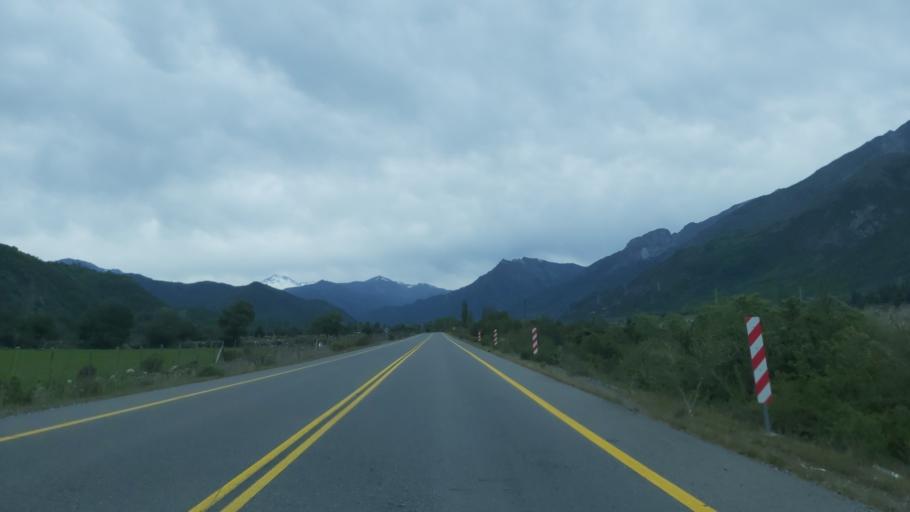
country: CL
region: Maule
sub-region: Provincia de Linares
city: Colbun
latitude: -35.7346
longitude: -71.0120
